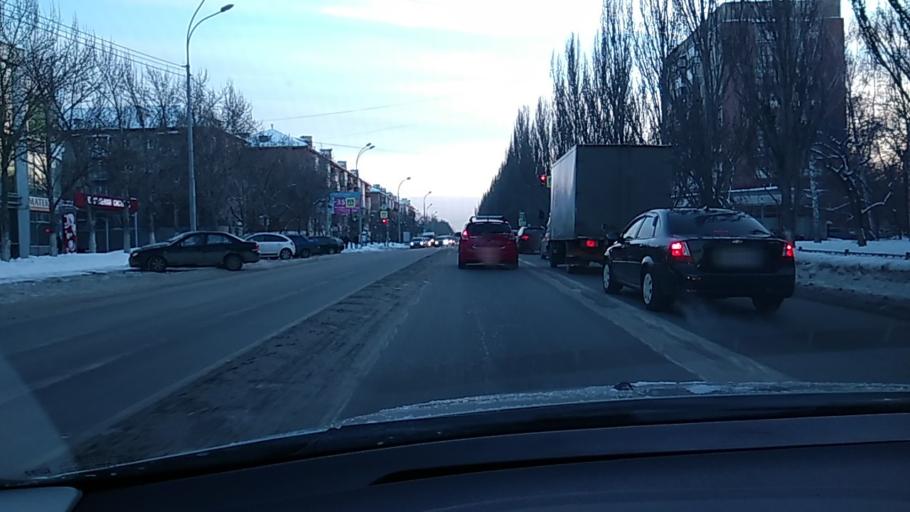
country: RU
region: Sverdlovsk
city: Yekaterinburg
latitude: 56.8338
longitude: 60.6348
